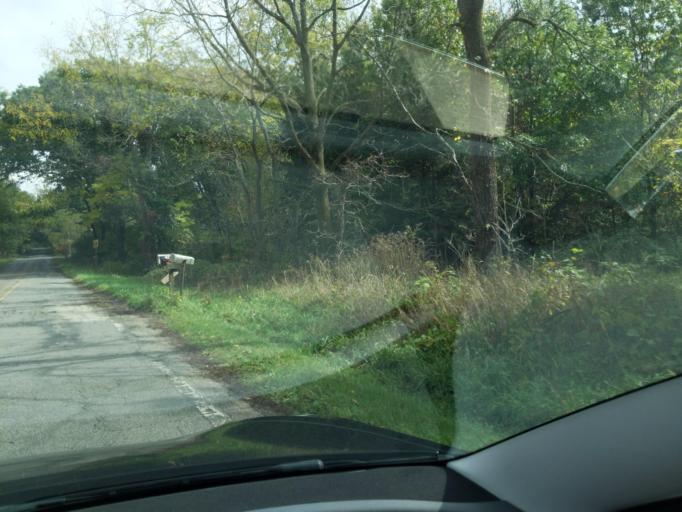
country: US
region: Michigan
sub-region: Ingham County
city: Leslie
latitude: 42.4115
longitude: -84.4685
